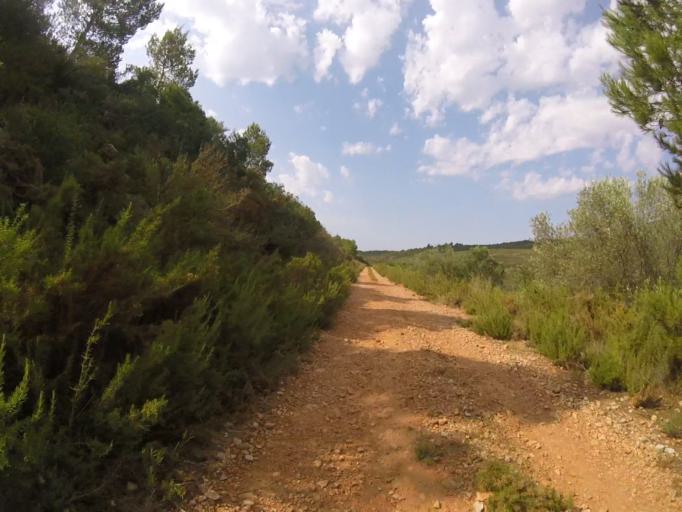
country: ES
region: Valencia
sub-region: Provincia de Castello
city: Alcala de Xivert
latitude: 40.3492
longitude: 0.1989
